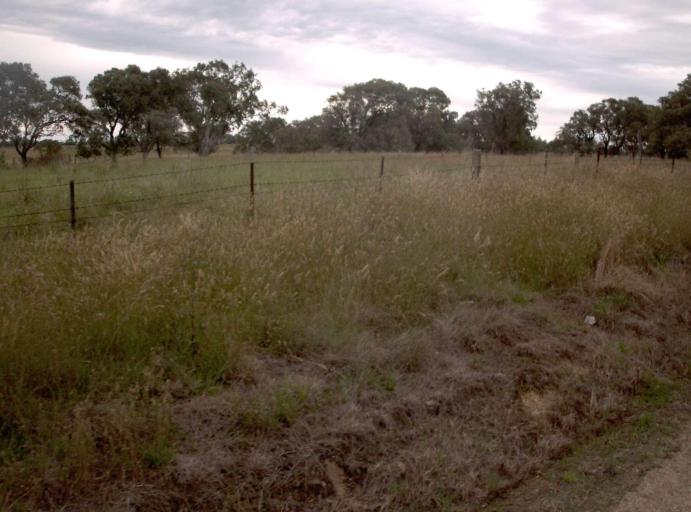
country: AU
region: Victoria
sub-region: Wellington
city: Sale
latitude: -38.0093
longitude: 147.1895
